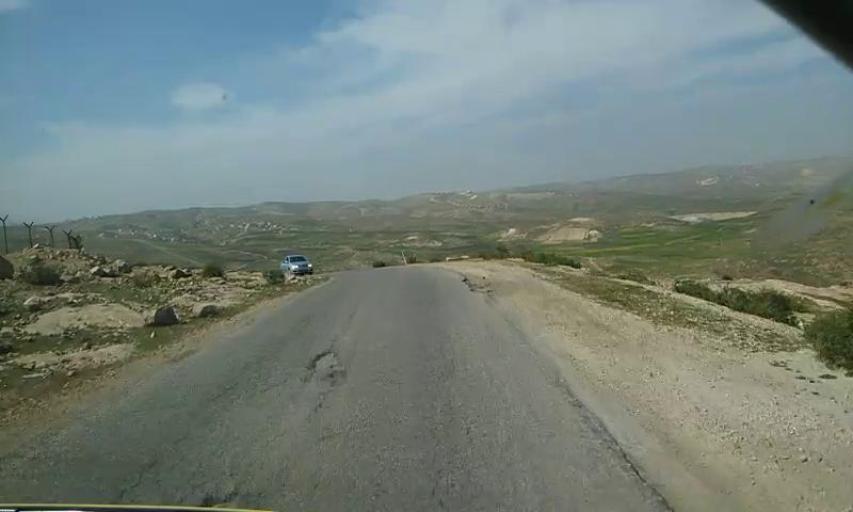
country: PS
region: West Bank
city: Khallat al Mayyah
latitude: 31.4340
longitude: 35.1849
